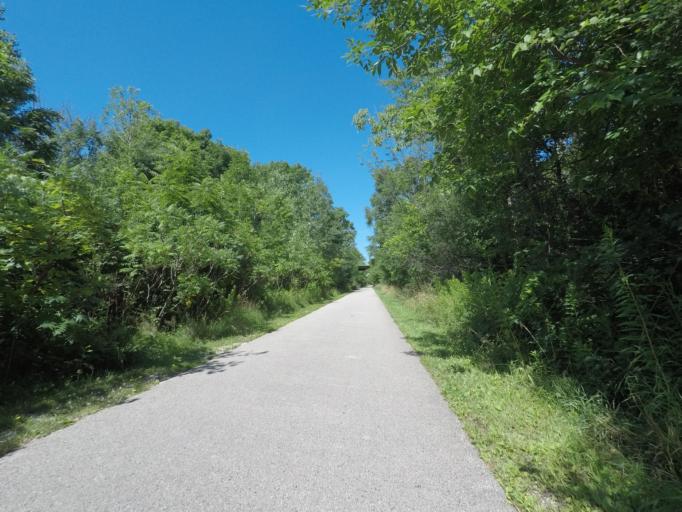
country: US
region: Wisconsin
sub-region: Milwaukee County
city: West Allis
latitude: 43.0245
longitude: -87.9983
